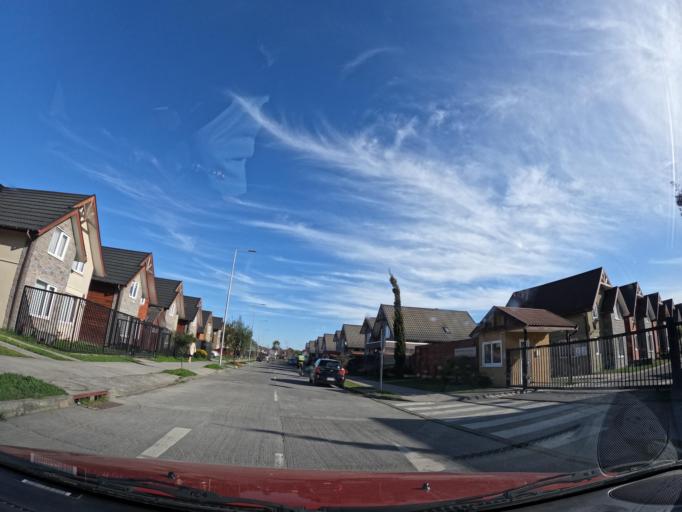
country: CL
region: Biobio
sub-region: Provincia de Concepcion
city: Concepcion
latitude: -36.7695
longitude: -73.0679
